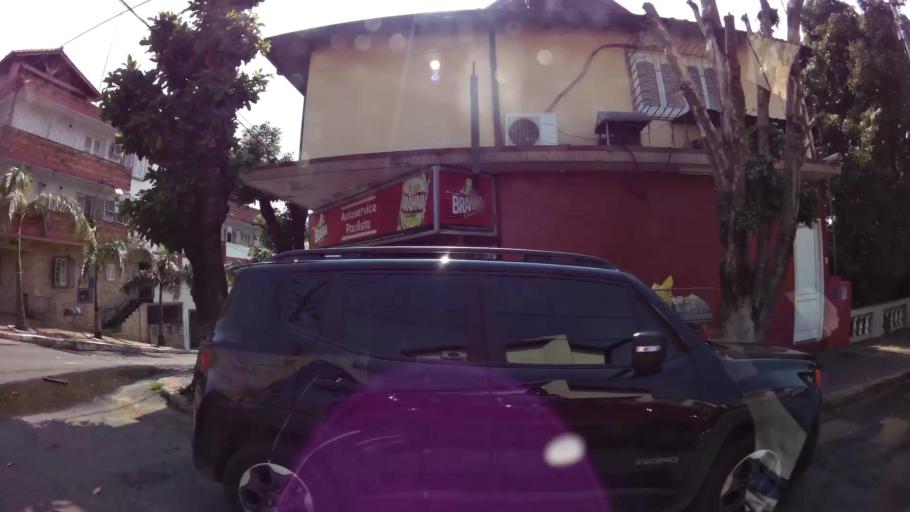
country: PY
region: Presidente Hayes
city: Nanawa
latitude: -25.2849
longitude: -57.6600
